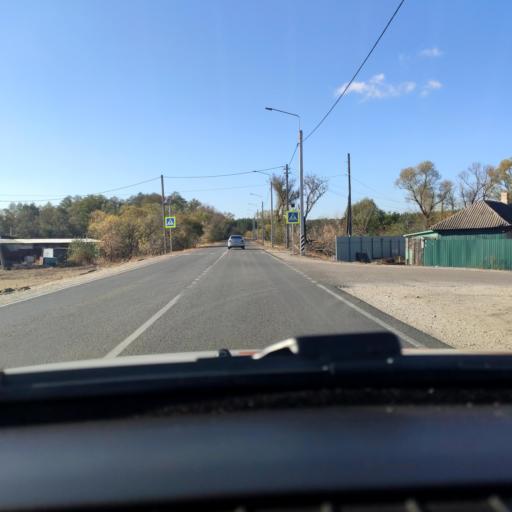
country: RU
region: Voronezj
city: Shilovo
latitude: 51.5290
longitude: 39.1530
